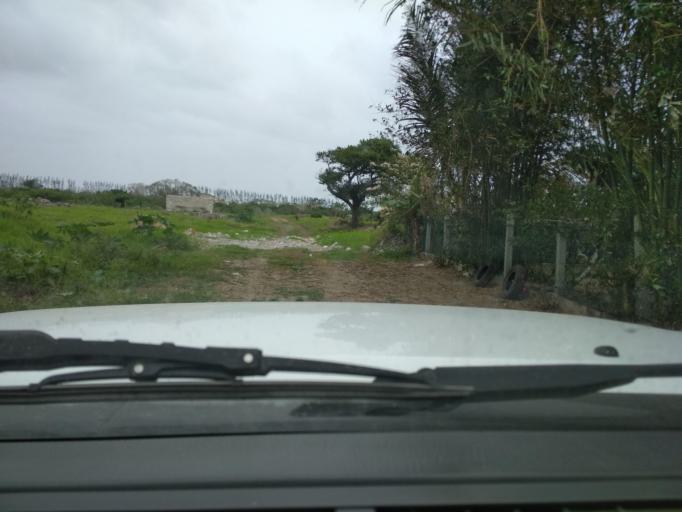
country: MX
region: Veracruz
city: Paso del Toro
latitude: 19.0422
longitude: -96.1308
